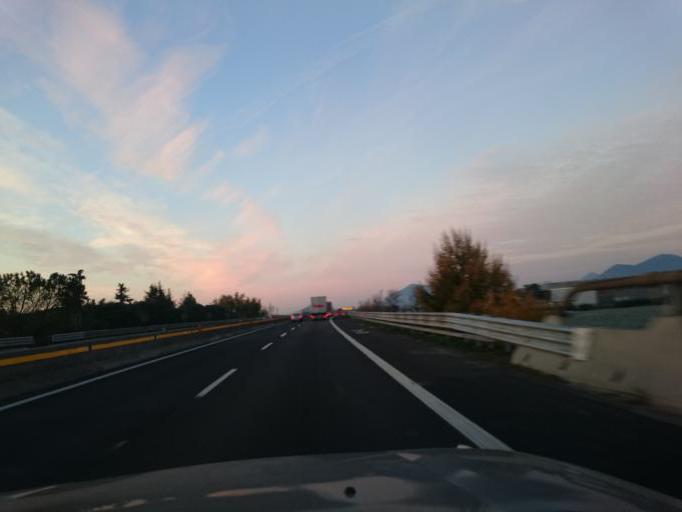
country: IT
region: Veneto
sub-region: Provincia di Padova
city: Carrara San Giorgio
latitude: 45.3040
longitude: 11.8176
